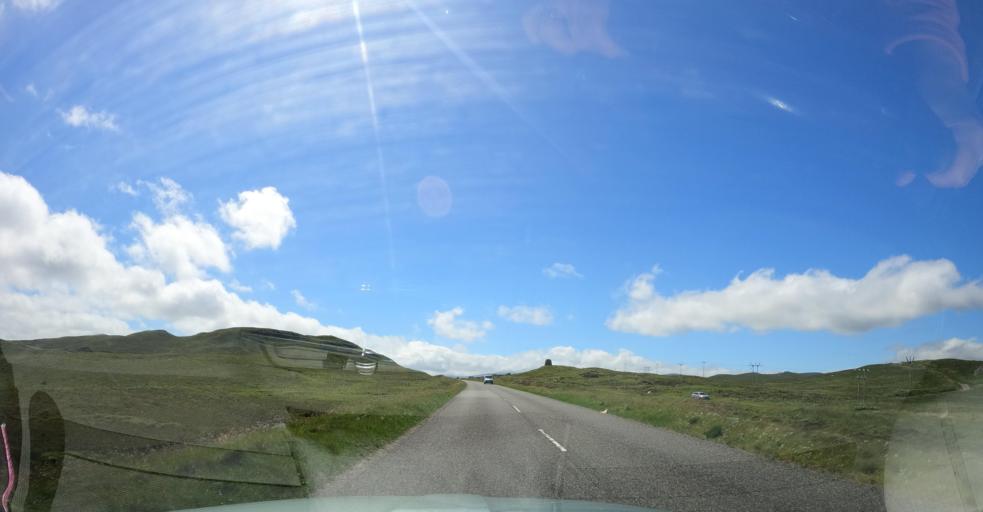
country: GB
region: Scotland
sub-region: Eilean Siar
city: Harris
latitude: 58.0810
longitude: -6.6466
